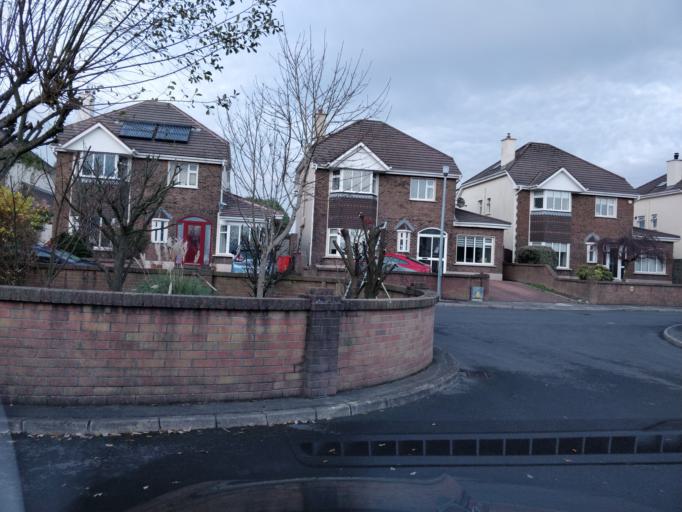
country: IE
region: Connaught
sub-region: County Galway
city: Bearna
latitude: 53.2666
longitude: -9.1115
